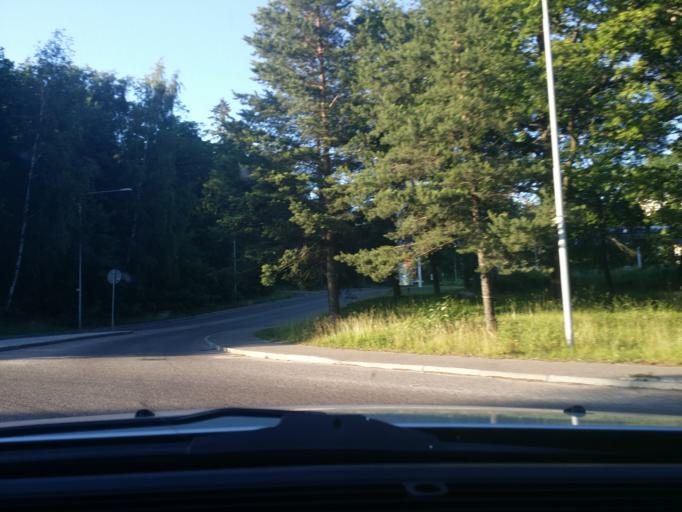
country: SE
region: Vaestmanland
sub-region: Vasteras
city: Vasteras
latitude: 59.6079
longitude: 16.5721
